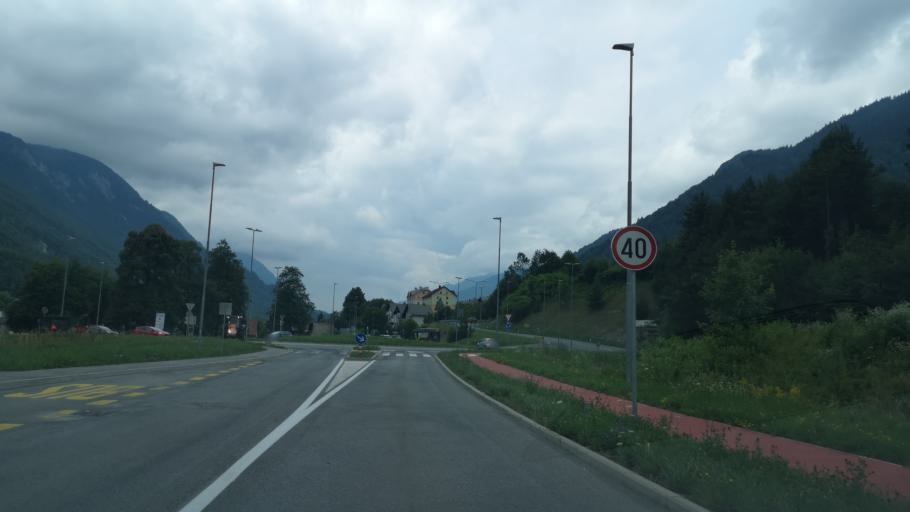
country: SI
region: Jesenice
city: Hrusica
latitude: 46.4468
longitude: 14.0167
